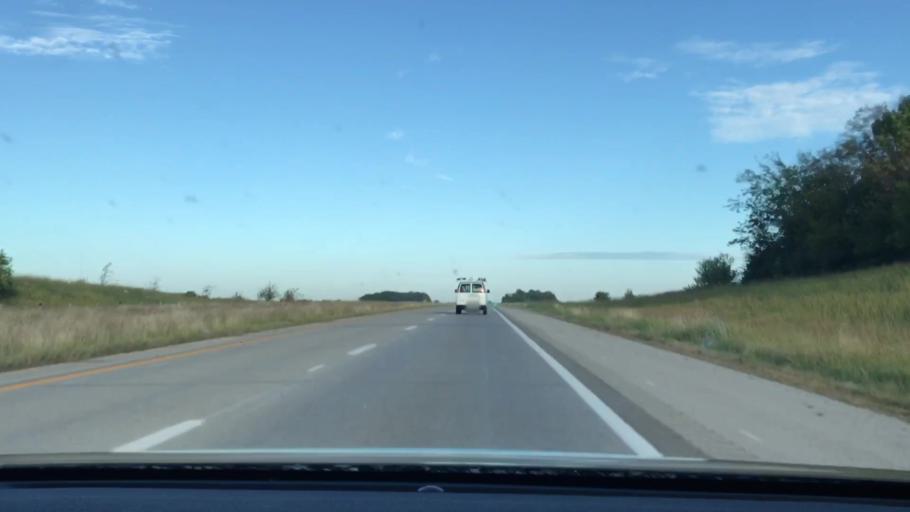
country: US
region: Kentucky
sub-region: Christian County
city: Hopkinsville
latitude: 36.8001
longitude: -87.6092
